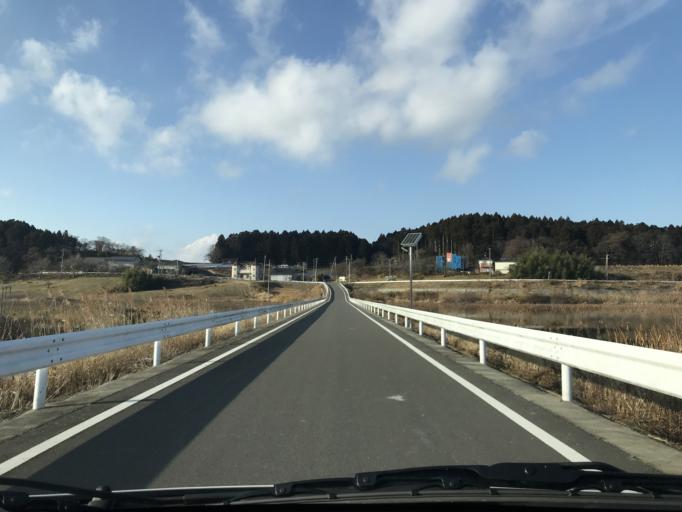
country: JP
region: Miyagi
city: Wakuya
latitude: 38.6820
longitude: 141.1156
